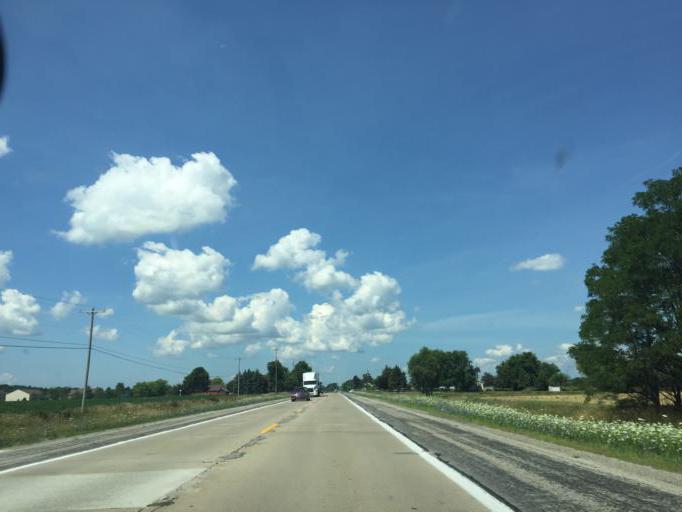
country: US
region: Ohio
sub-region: Lucas County
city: Sylvania
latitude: 41.7972
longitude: -83.7095
